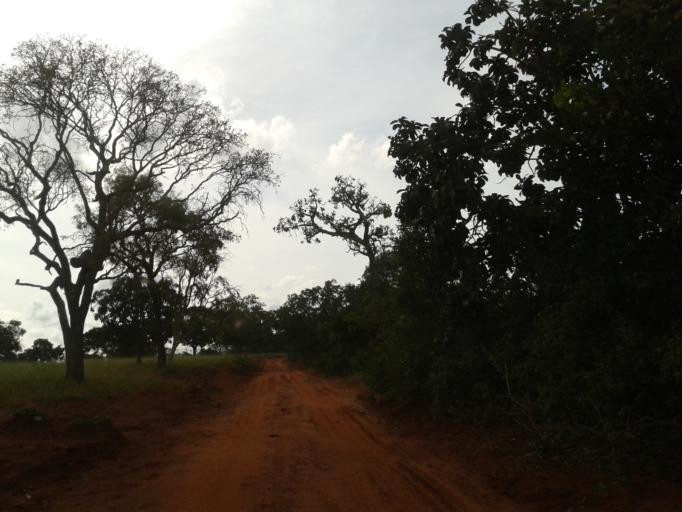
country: BR
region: Minas Gerais
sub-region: Campina Verde
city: Campina Verde
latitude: -19.4405
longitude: -49.6179
